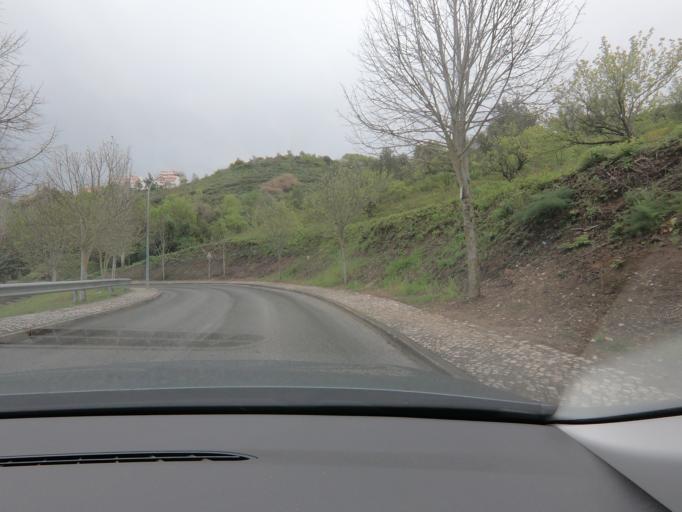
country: PT
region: Lisbon
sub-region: Alenquer
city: Alenquer
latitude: 39.0506
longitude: -9.0092
